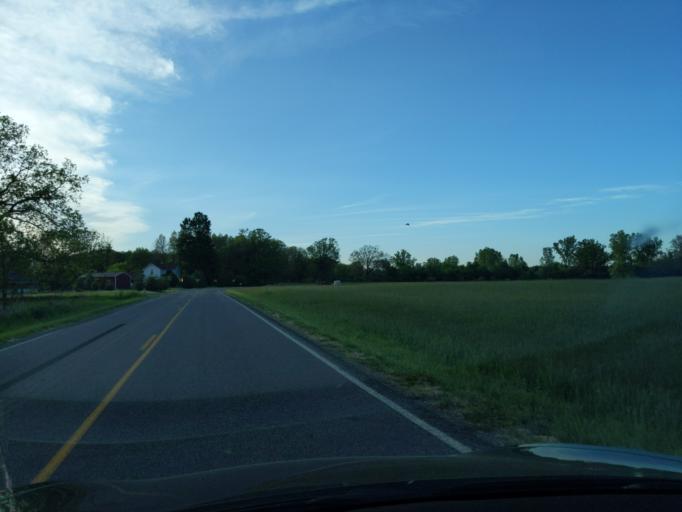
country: US
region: Michigan
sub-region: Ingham County
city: Leslie
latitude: 42.4670
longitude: -84.3165
